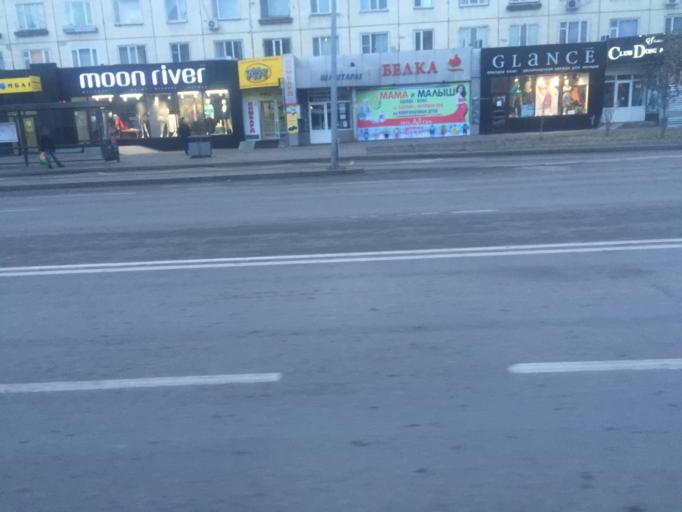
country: KZ
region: Astana Qalasy
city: Astana
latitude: 51.1705
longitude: 71.4126
